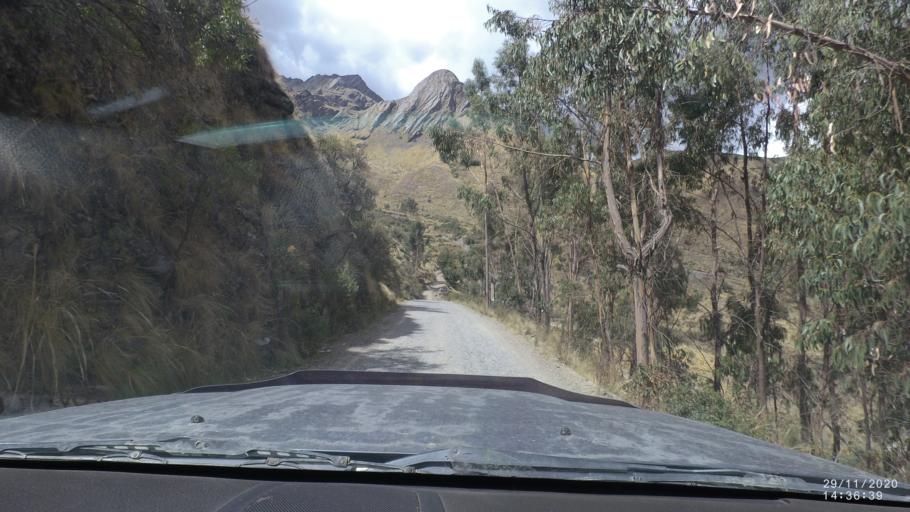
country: BO
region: Cochabamba
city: Sipe Sipe
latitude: -17.2695
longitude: -66.3291
